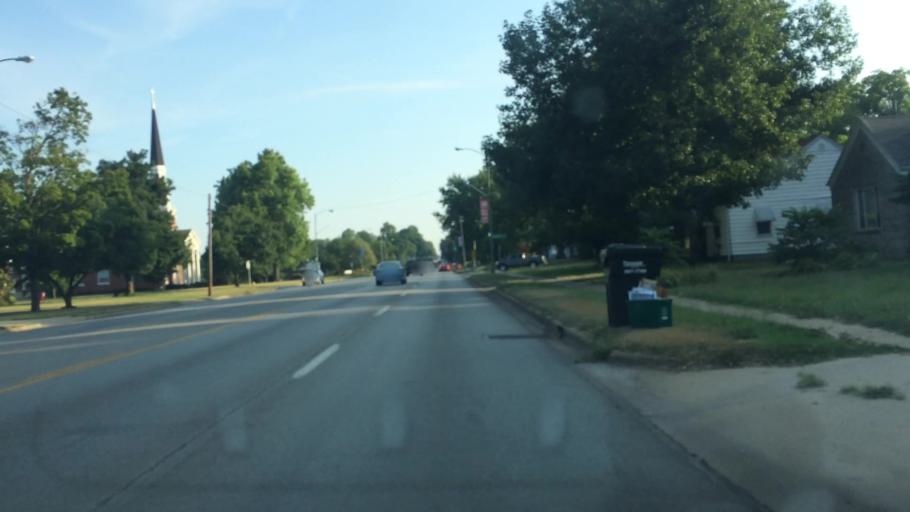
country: US
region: Missouri
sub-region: Greene County
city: Springfield
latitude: 37.1845
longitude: -93.2765
